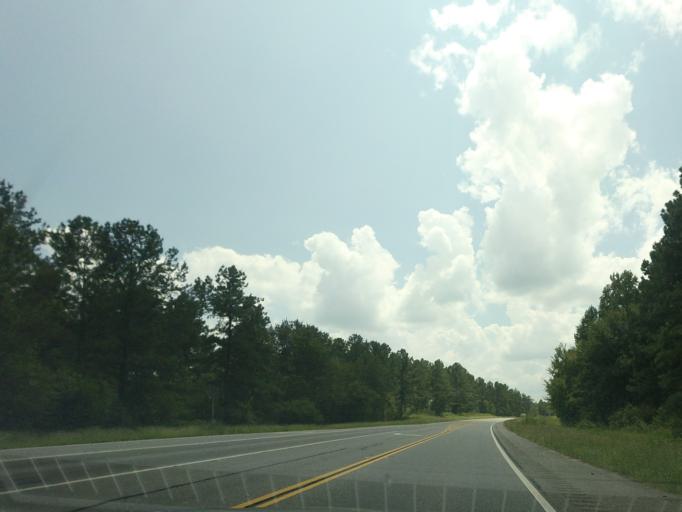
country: US
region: Georgia
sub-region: Bleckley County
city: Cochran
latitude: 32.3832
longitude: -83.3276
